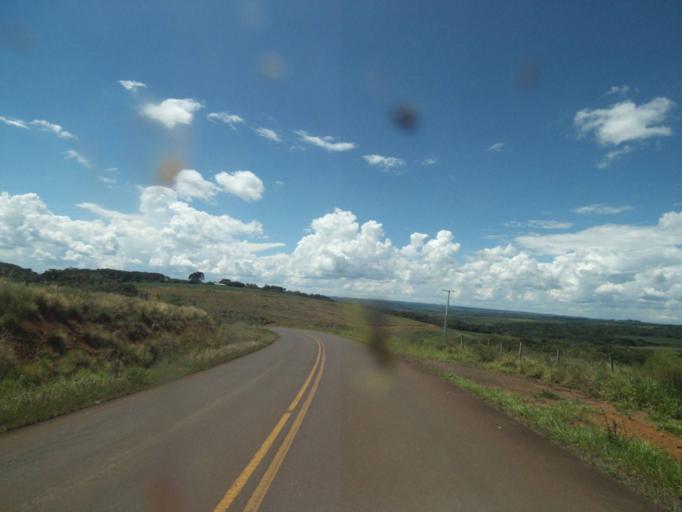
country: BR
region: Parana
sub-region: Pinhao
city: Pinhao
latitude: -25.7974
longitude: -52.0748
